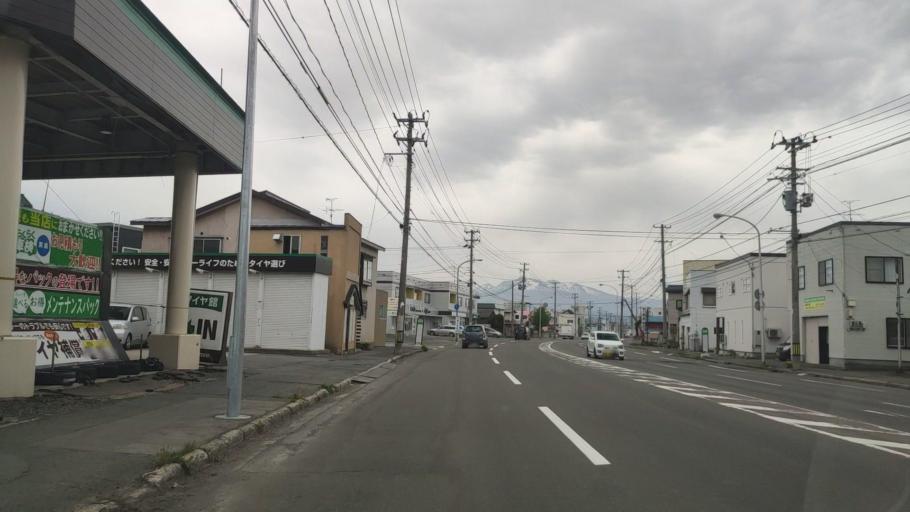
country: JP
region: Aomori
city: Aomori Shi
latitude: 40.8182
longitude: 140.7742
